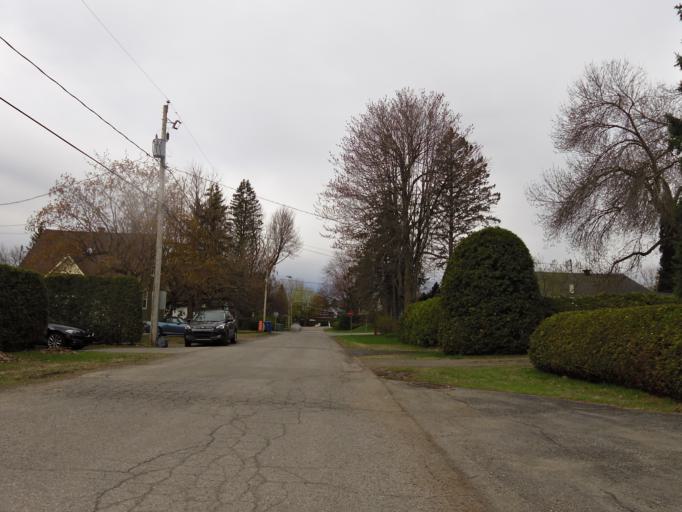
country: CA
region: Quebec
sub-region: Laurentides
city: Oka
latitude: 45.4646
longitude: -74.0763
